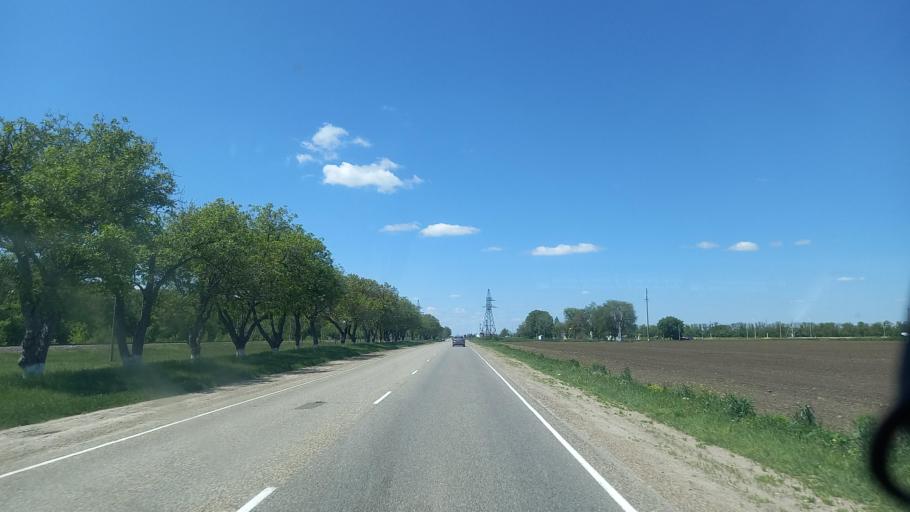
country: RU
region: Krasnodarskiy
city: Tbilisskaya
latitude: 45.3658
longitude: 40.1332
